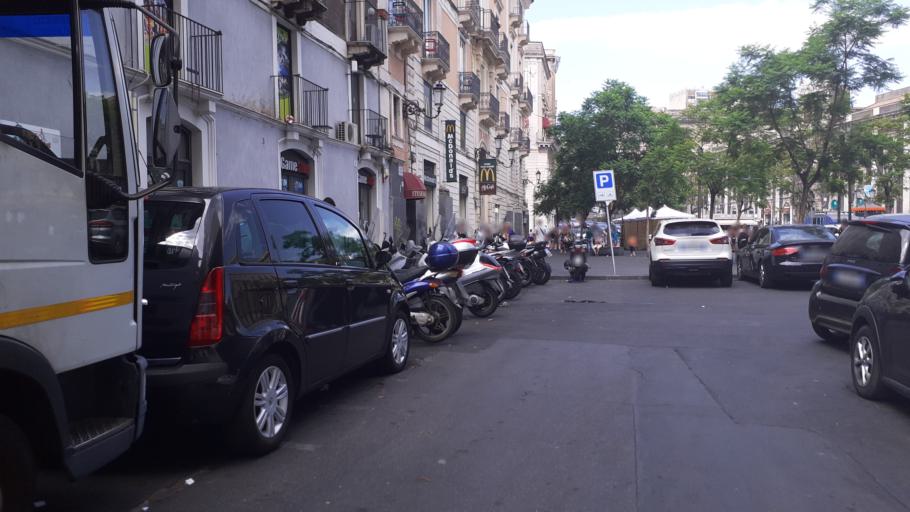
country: IT
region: Sicily
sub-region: Catania
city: Catania
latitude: 37.5071
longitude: 15.0872
